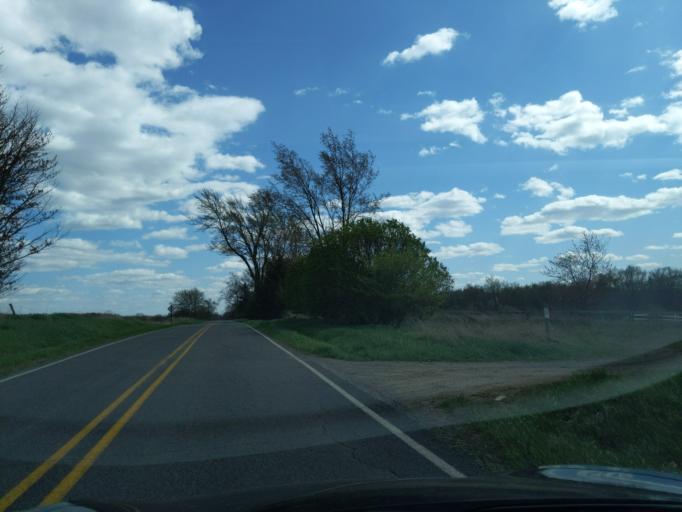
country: US
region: Michigan
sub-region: Ingham County
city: Leslie
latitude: 42.4066
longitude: -84.5416
